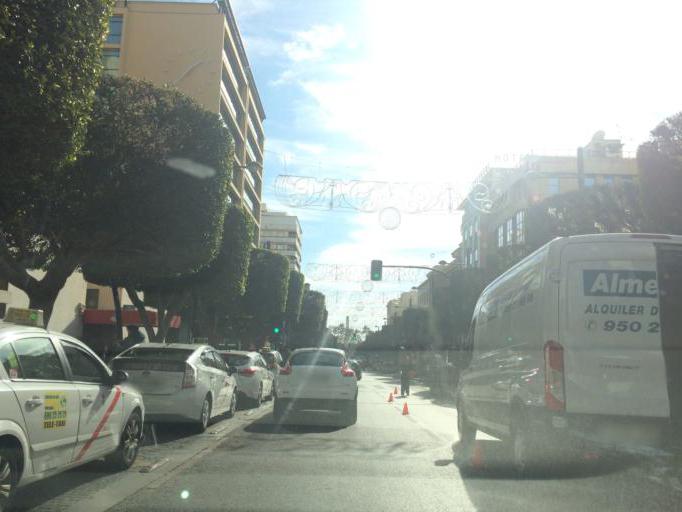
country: ES
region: Andalusia
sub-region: Provincia de Almeria
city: Almeria
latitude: 36.8374
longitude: -2.4632
